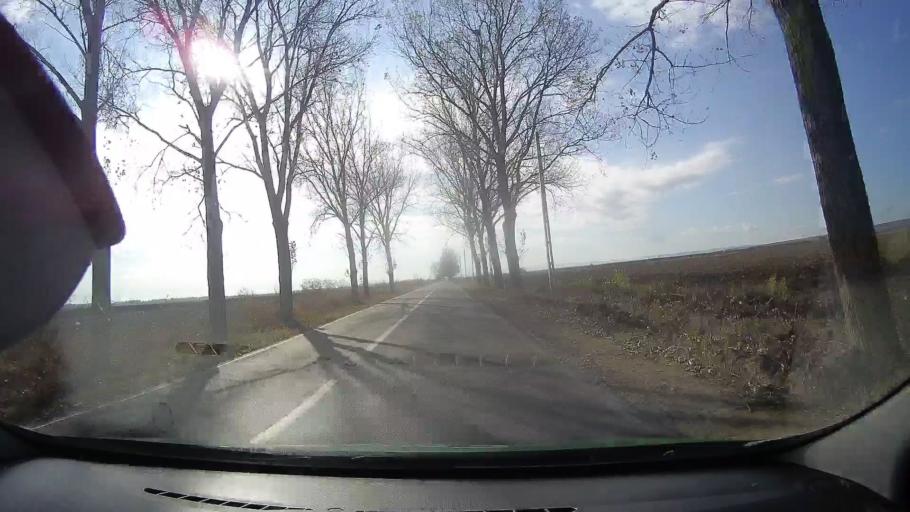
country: RO
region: Tulcea
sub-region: Comuna Valea Nucarilor
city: Agighiol
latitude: 44.9955
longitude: 28.8865
